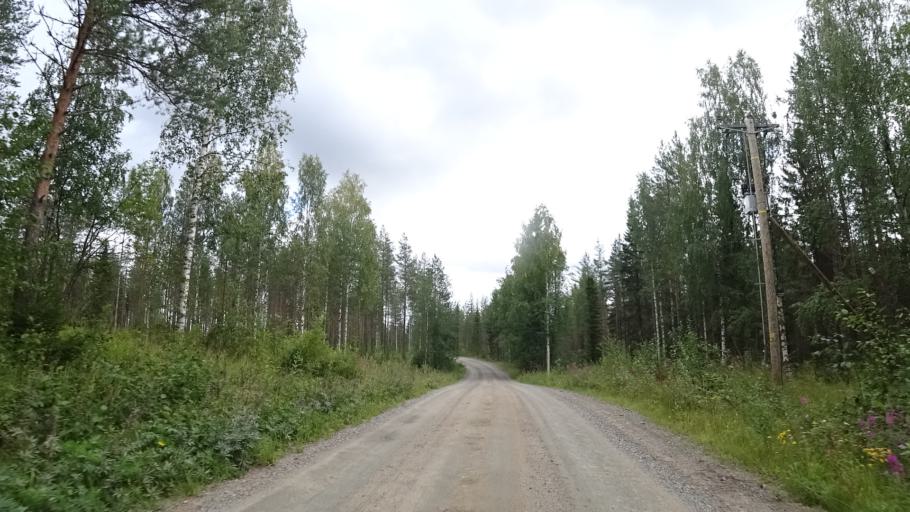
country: FI
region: North Karelia
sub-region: Joensuu
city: Ilomantsi
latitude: 62.9297
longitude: 31.3170
